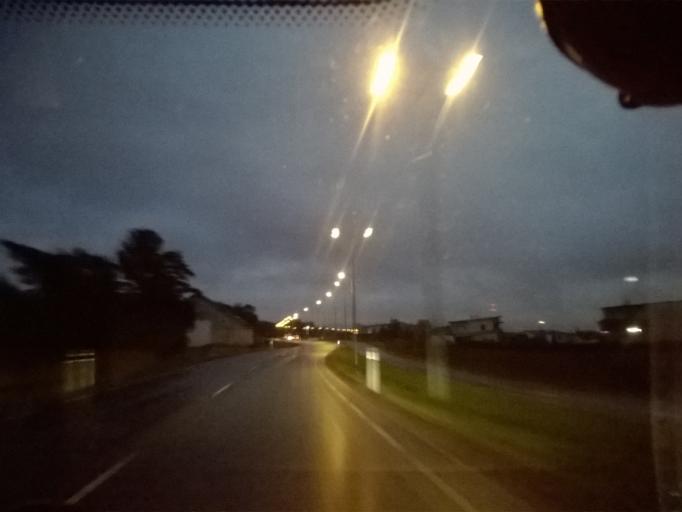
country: EE
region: Harju
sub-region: Viimsi vald
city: Viimsi
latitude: 59.5067
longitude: 24.8616
